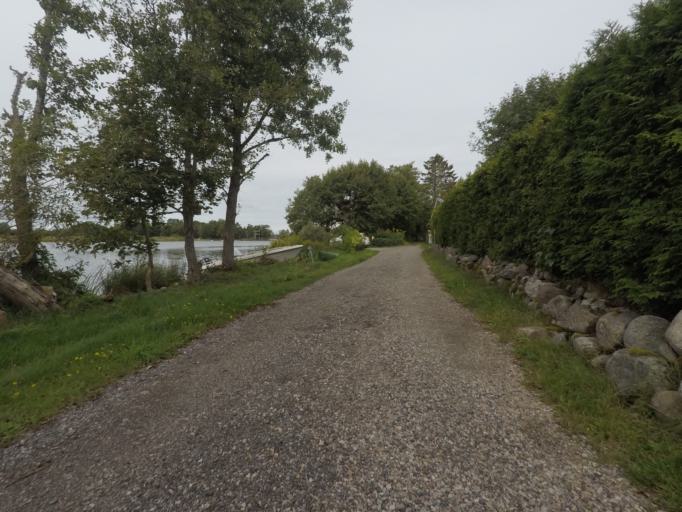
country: SE
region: Vaestmanland
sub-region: Kungsors Kommun
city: Kungsoer
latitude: 59.4685
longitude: 16.0717
